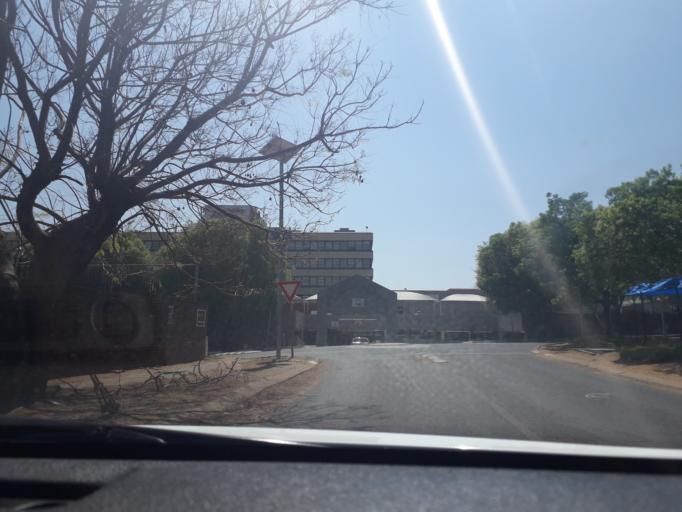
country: ZA
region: Gauteng
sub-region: City of Johannesburg Metropolitan Municipality
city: Roodepoort
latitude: -26.1292
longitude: 27.9674
